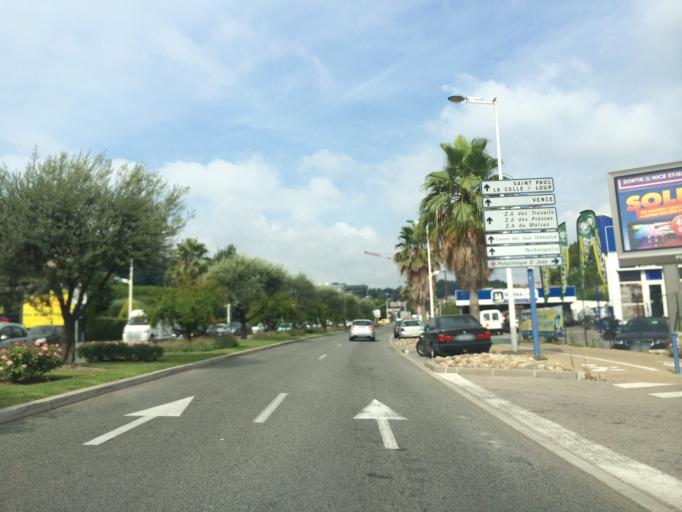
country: FR
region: Provence-Alpes-Cote d'Azur
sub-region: Departement des Alpes-Maritimes
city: Cagnes-sur-Mer
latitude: 43.6601
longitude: 7.1400
